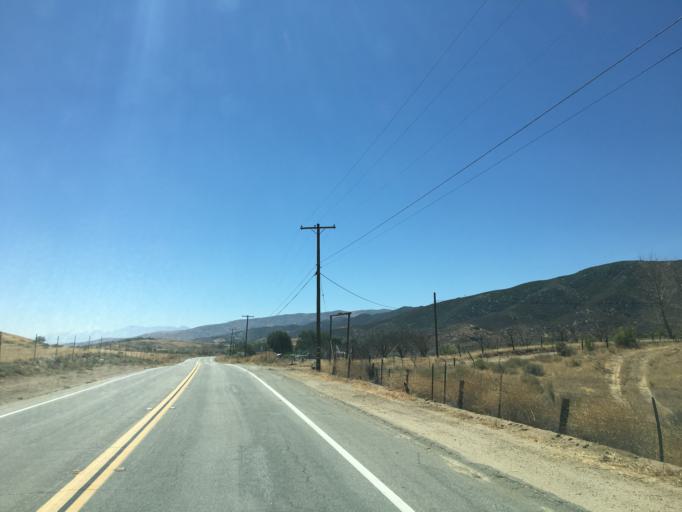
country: US
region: California
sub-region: Los Angeles County
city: Leona Valley
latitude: 34.6354
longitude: -118.3398
